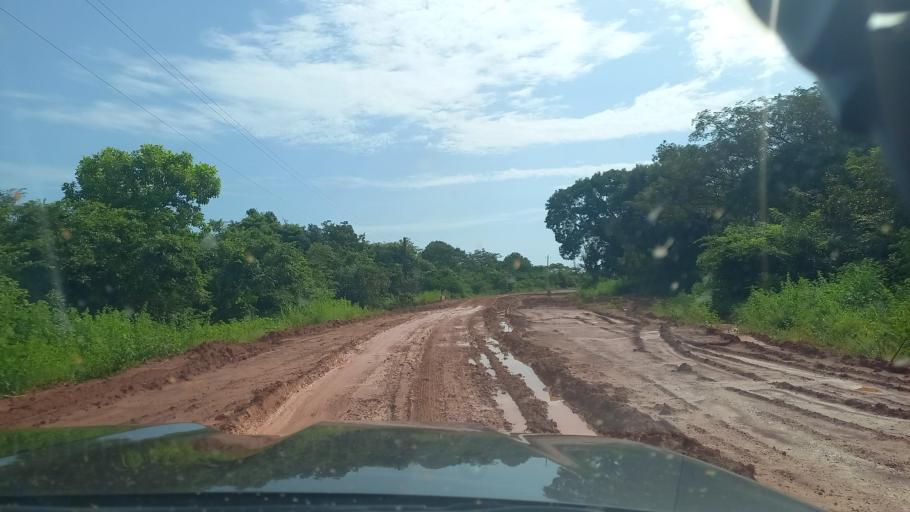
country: SN
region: Ziguinchor
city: Ziguinchor
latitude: 12.6715
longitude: -16.2182
